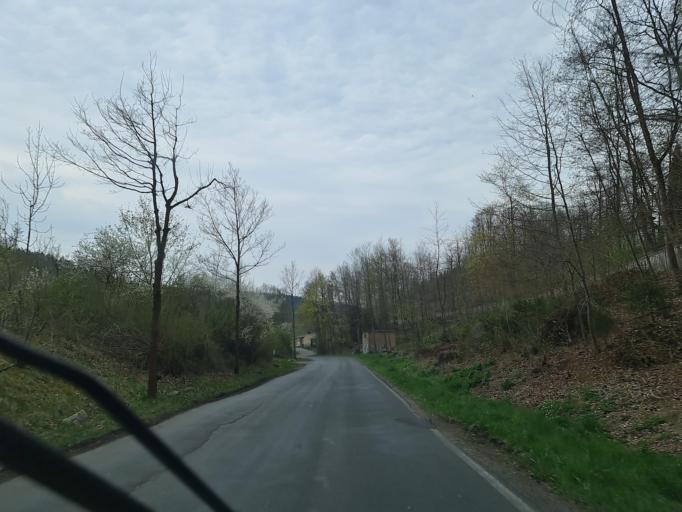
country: DE
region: Saxony
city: Falkenstein
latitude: 50.4703
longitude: 12.3769
